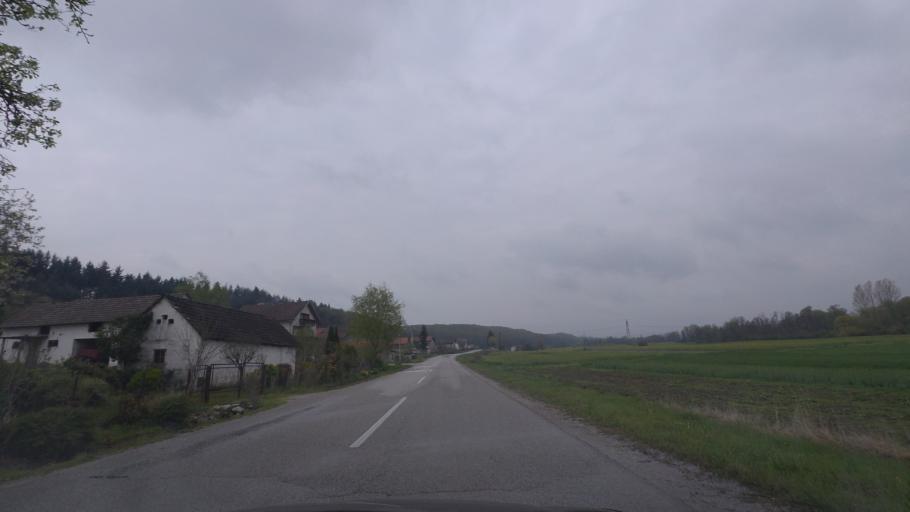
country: HR
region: Zagrebacka
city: Jastrebarsko
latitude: 45.6206
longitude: 15.5665
